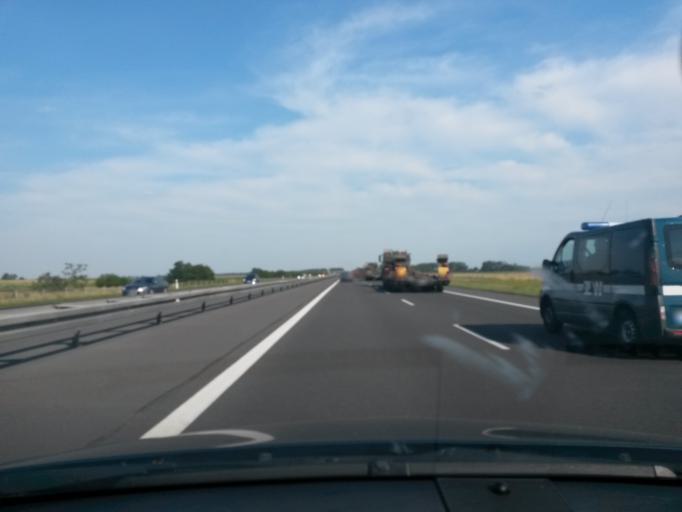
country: PL
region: Greater Poland Voivodeship
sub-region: Powiat wrzesinski
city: Wrzesnia
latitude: 52.2988
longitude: 17.6335
